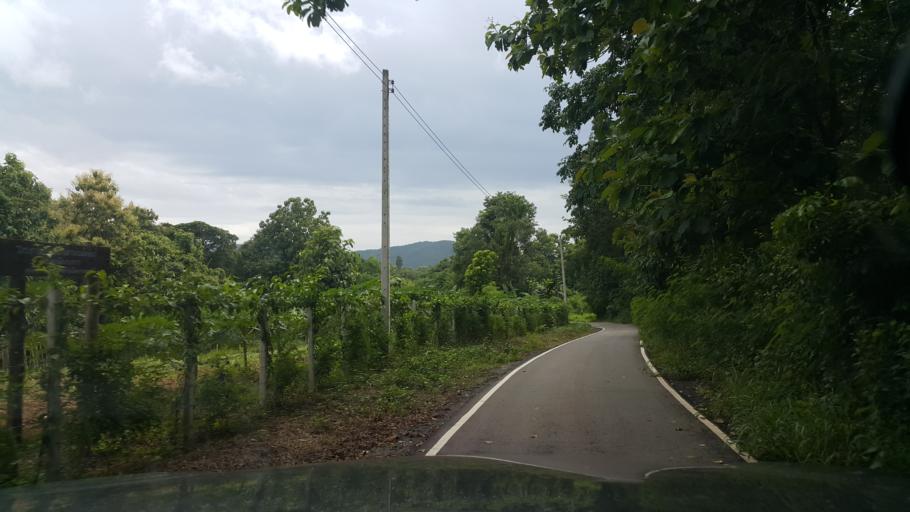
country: TH
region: Chiang Mai
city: Mae On
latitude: 18.8441
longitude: 99.2241
